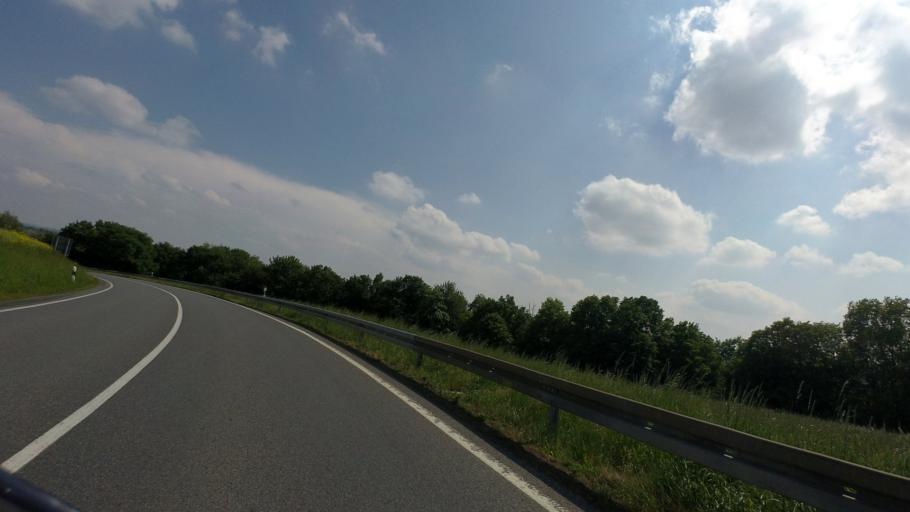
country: DE
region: Saxony
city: Weissenberg
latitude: 51.1929
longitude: 14.6726
